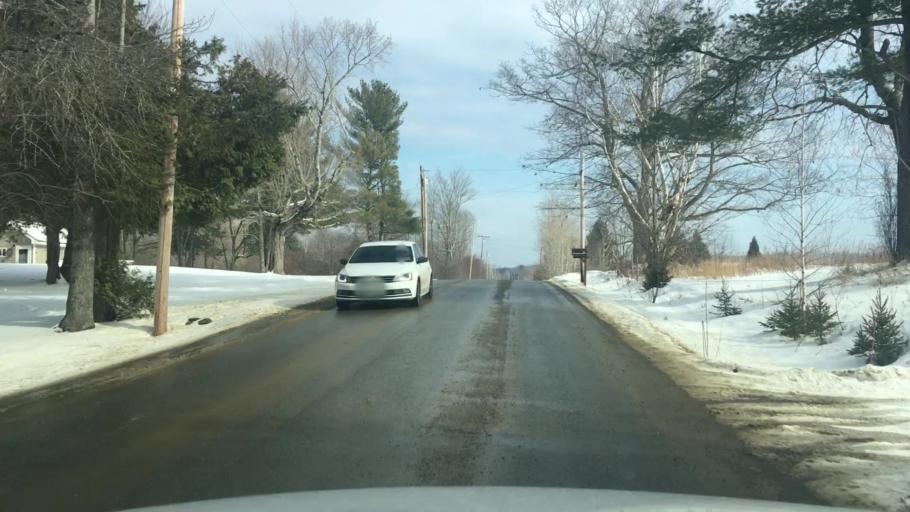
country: US
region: Maine
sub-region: Penobscot County
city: Hermon
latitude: 44.7569
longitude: -68.9697
